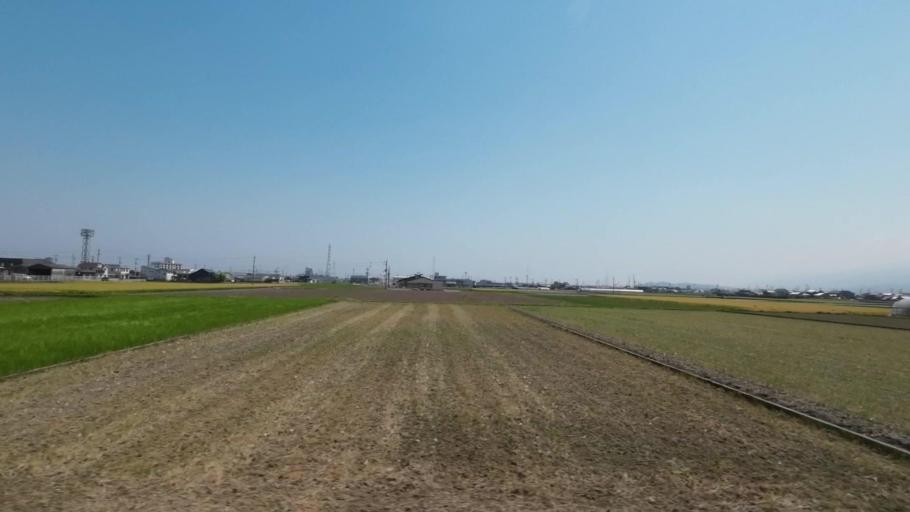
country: JP
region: Ehime
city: Saijo
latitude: 33.9165
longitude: 133.0973
